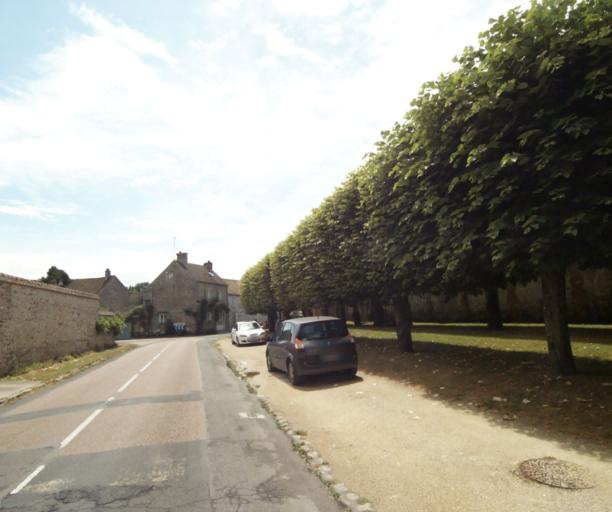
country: FR
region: Ile-de-France
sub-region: Departement de Seine-et-Marne
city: Cely
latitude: 48.4456
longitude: 2.5506
